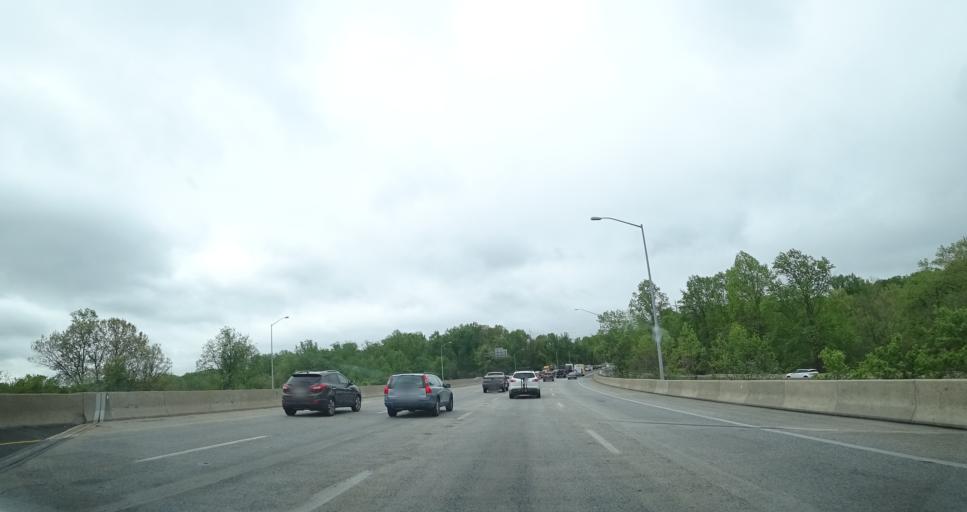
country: US
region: Maryland
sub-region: Montgomery County
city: Cabin John
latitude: 38.9862
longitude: -77.1580
